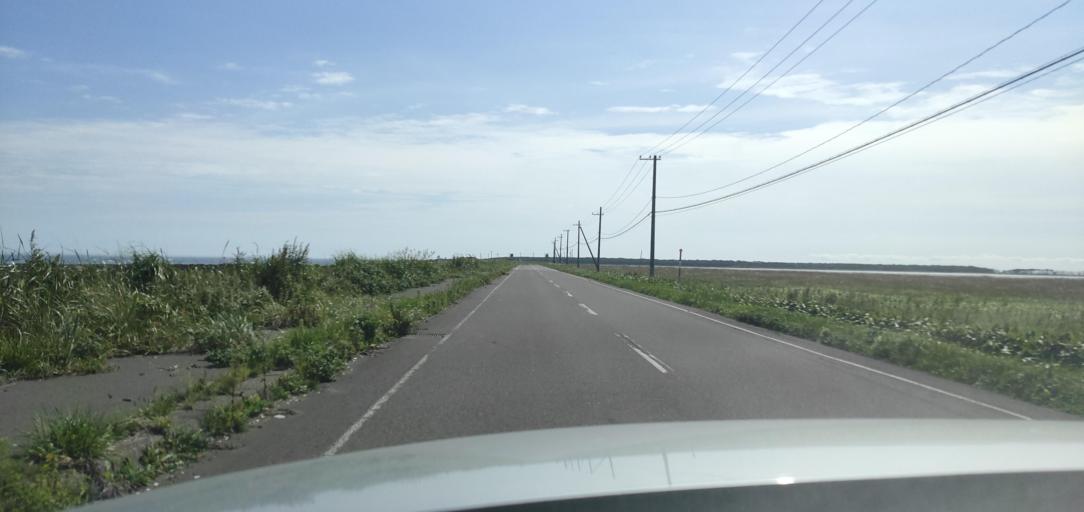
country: JP
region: Hokkaido
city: Shibetsu
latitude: 43.6155
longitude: 145.2422
